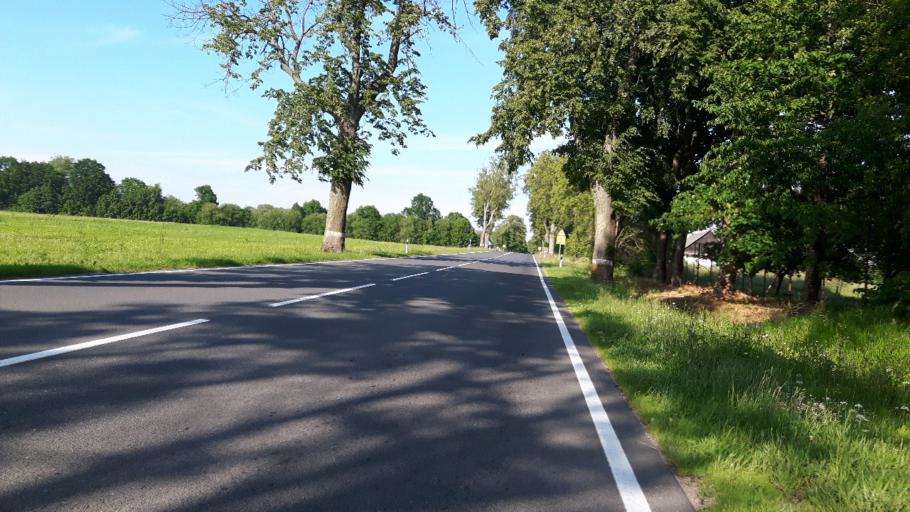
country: RU
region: Kaliningrad
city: Mamonovo
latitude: 54.4924
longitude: 20.0597
